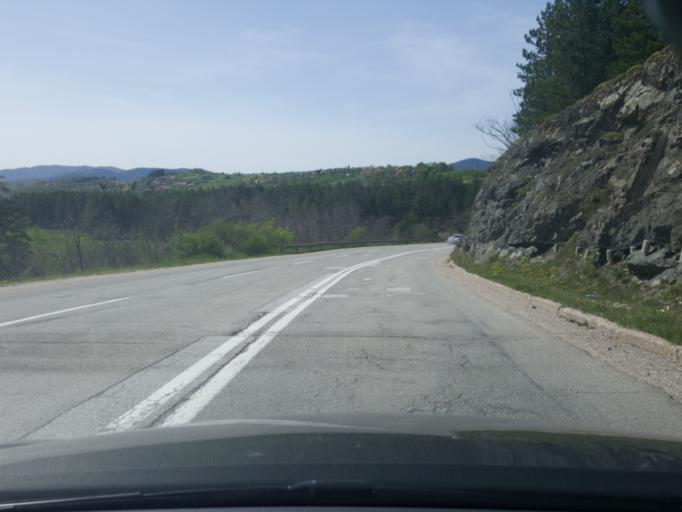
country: RS
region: Central Serbia
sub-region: Zlatiborski Okrug
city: Cajetina
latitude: 43.8353
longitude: 19.6077
